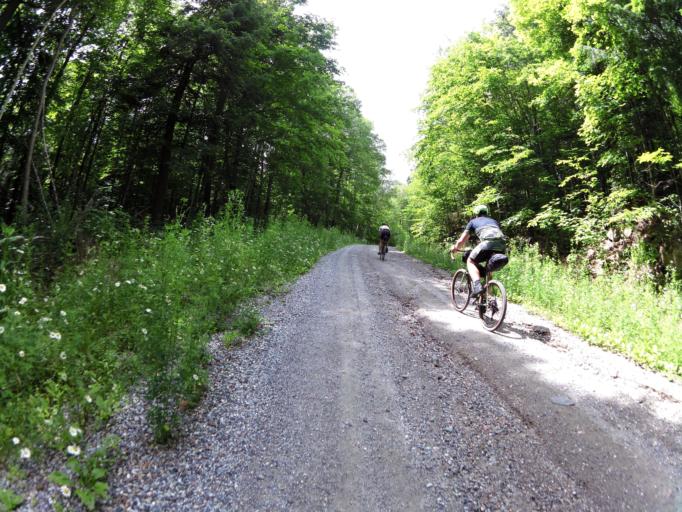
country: CA
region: Ontario
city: Perth
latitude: 45.0186
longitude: -76.5794
